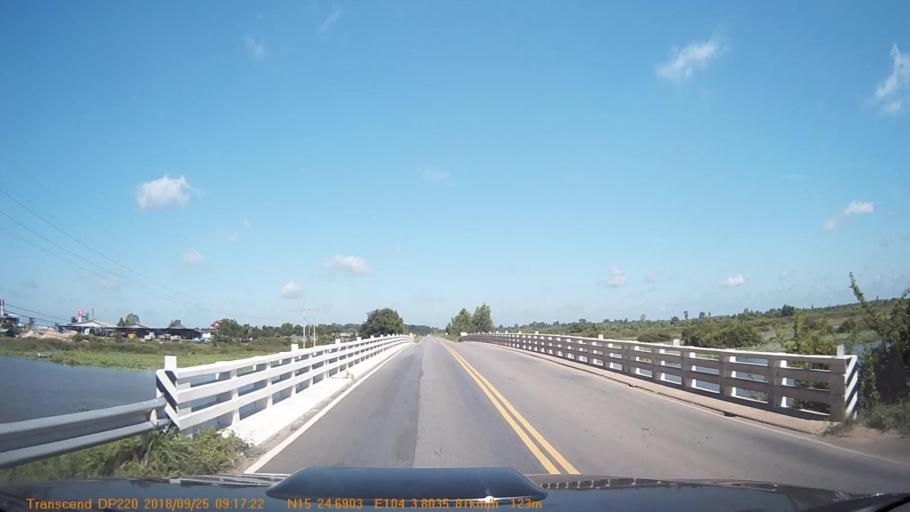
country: TH
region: Sisaket
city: Sila Lat
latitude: 15.4115
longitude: 104.0635
